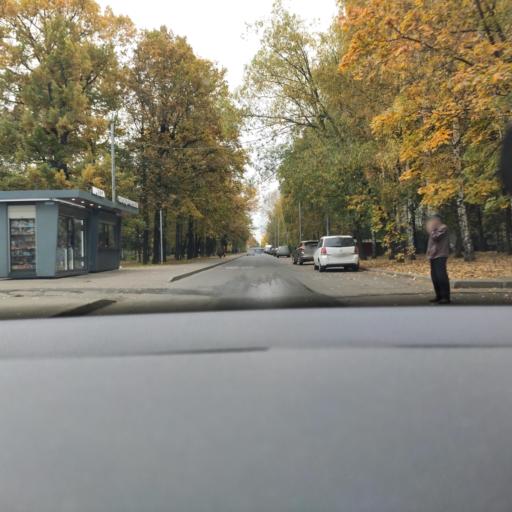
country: RU
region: Moscow
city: Lianozovo
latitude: 55.8958
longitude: 37.5766
